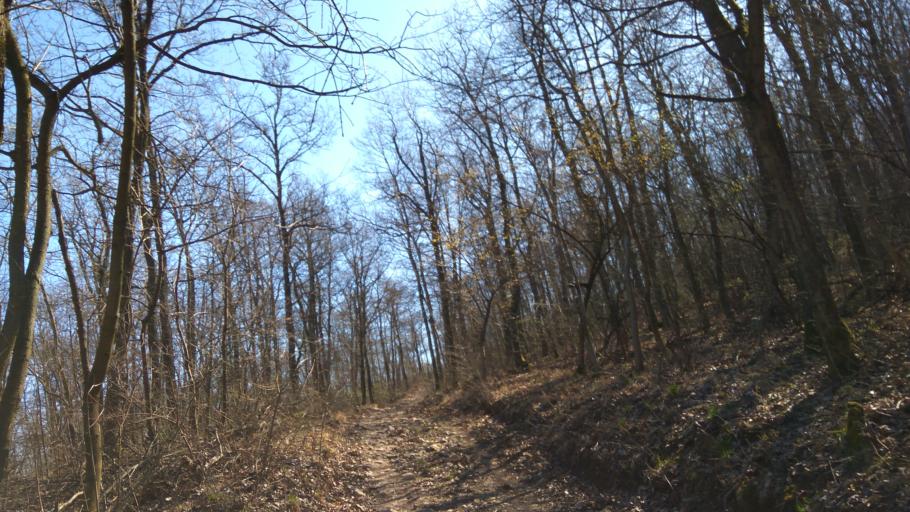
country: HU
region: Pest
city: Csobanka
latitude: 47.6370
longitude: 18.9790
